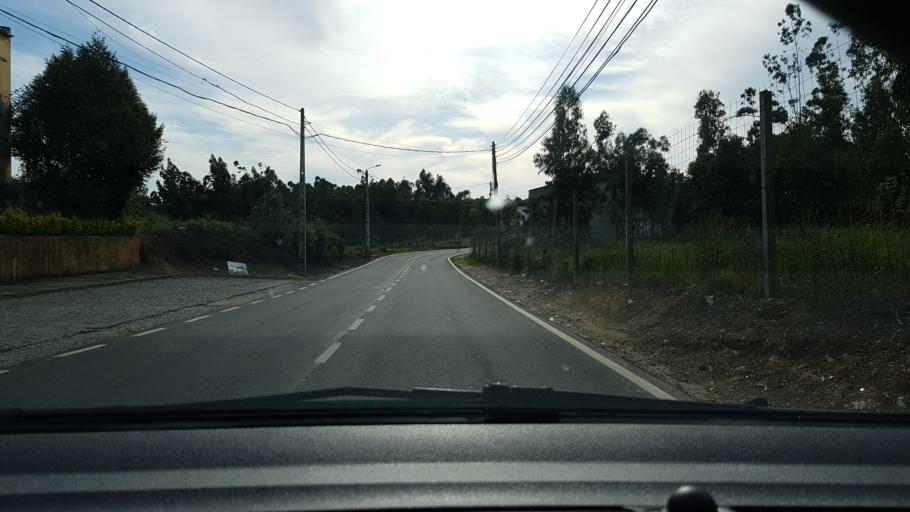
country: PT
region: Porto
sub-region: Gondomar
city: Baguim do Monte
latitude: 41.1927
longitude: -8.5458
